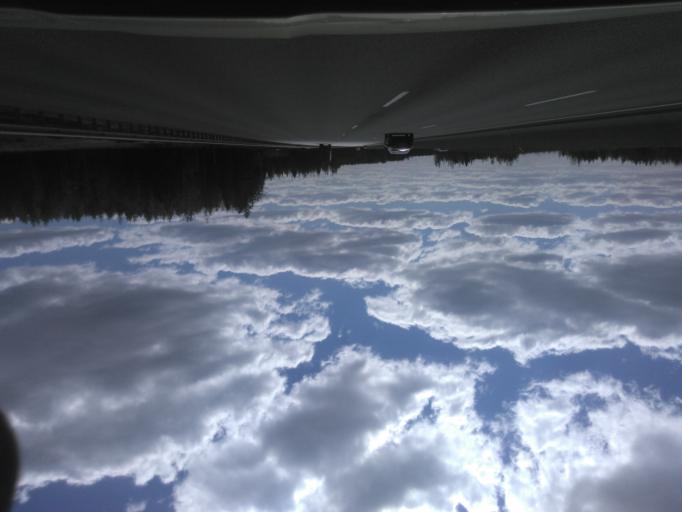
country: RU
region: Moskovskaya
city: Skhodnya
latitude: 55.9890
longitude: 37.3046
